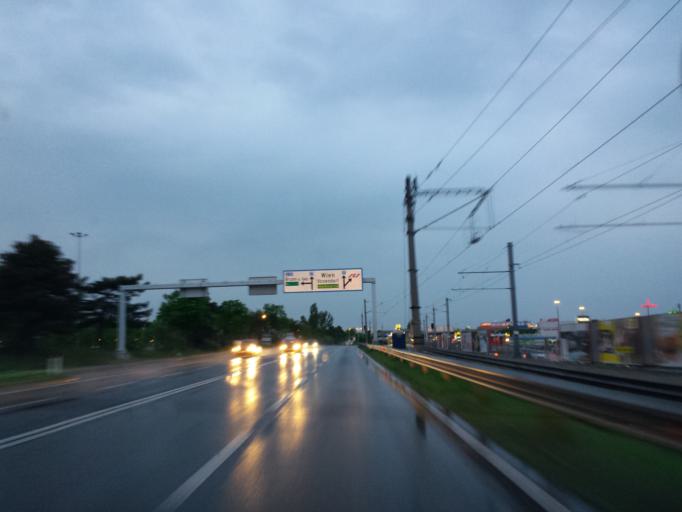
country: AT
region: Lower Austria
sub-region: Politischer Bezirk Modling
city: Vosendorf
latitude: 48.1100
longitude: 16.3154
